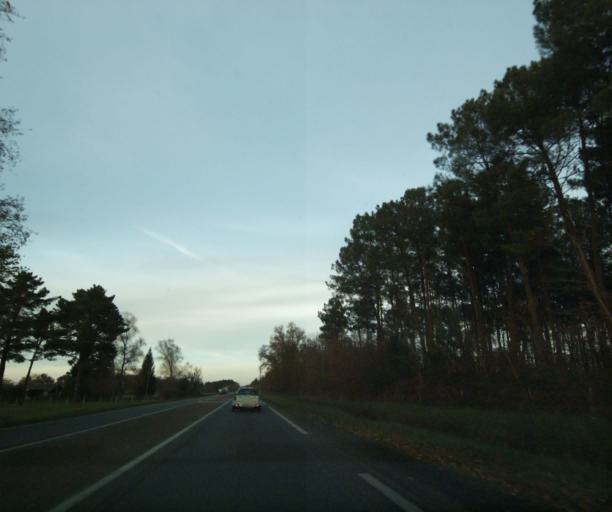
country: FR
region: Aquitaine
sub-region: Departement de la Gironde
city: Bazas
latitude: 44.4550
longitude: -0.2330
